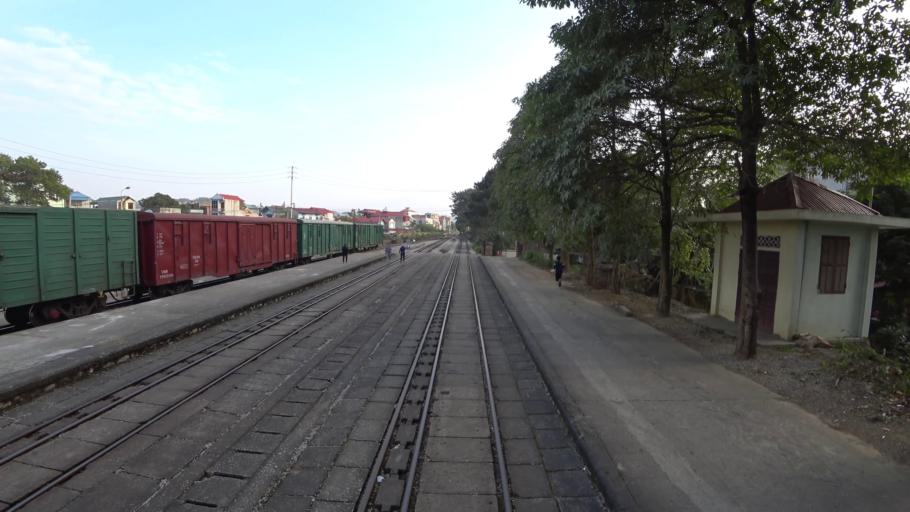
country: VN
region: Lang Son
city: Thanh Pho Lang Son
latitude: 21.8577
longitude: 106.7681
